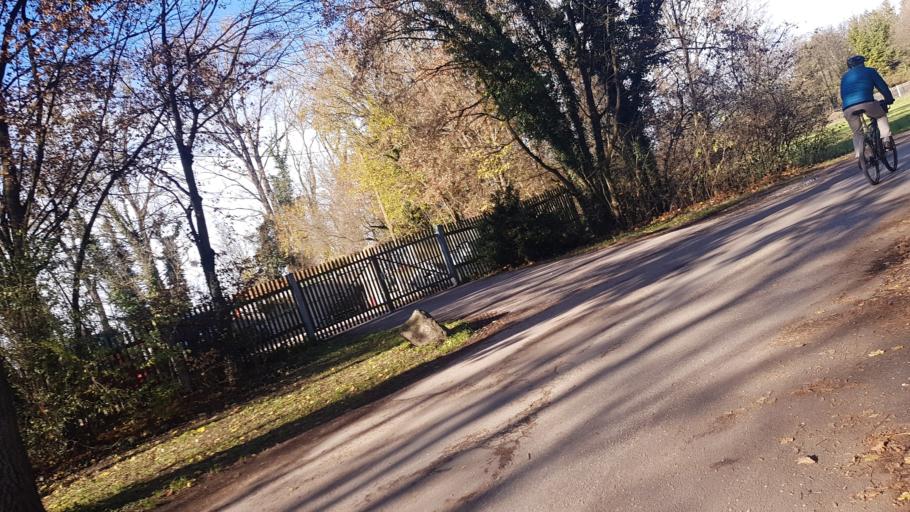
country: DE
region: Bavaria
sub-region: Upper Bavaria
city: Karlsfeld
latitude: 48.2141
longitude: 11.5213
